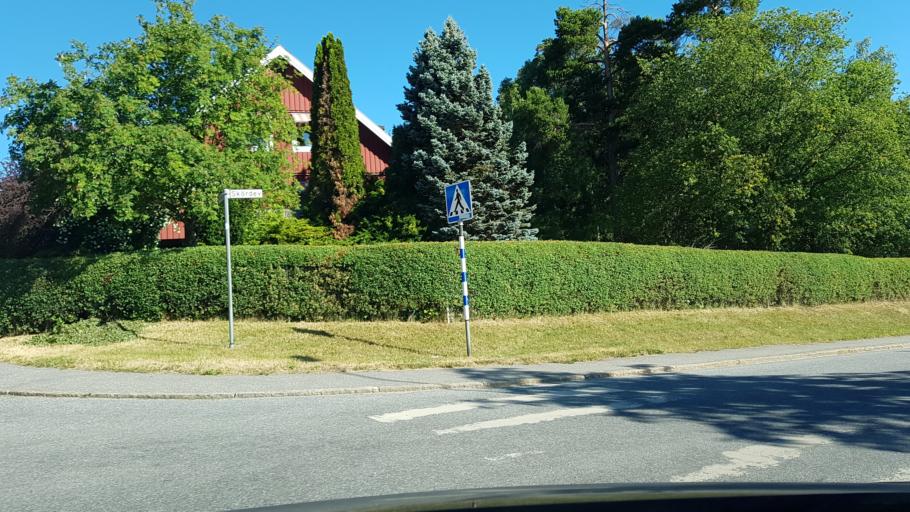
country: SE
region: Stockholm
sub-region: Jarfalla Kommun
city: Jakobsberg
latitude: 59.4144
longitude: 17.8199
